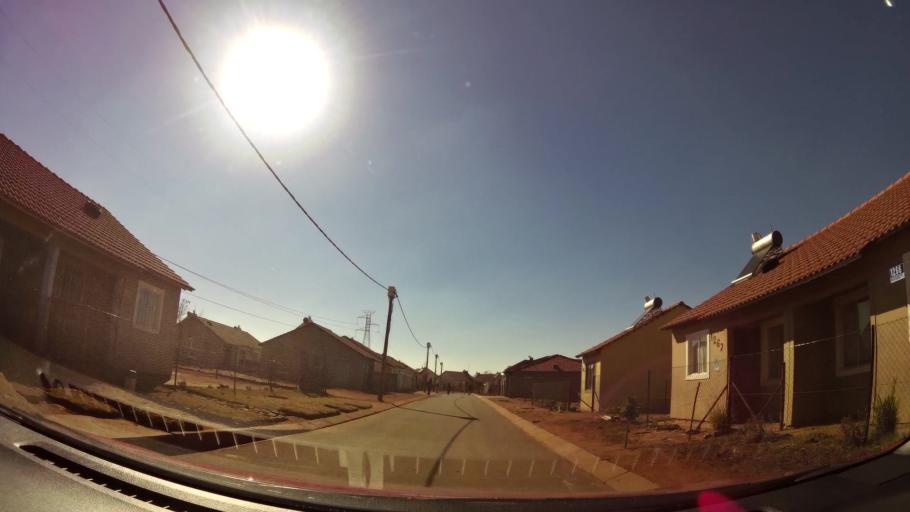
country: ZA
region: Gauteng
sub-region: City of Johannesburg Metropolitan Municipality
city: Soweto
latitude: -26.2331
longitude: 27.8000
